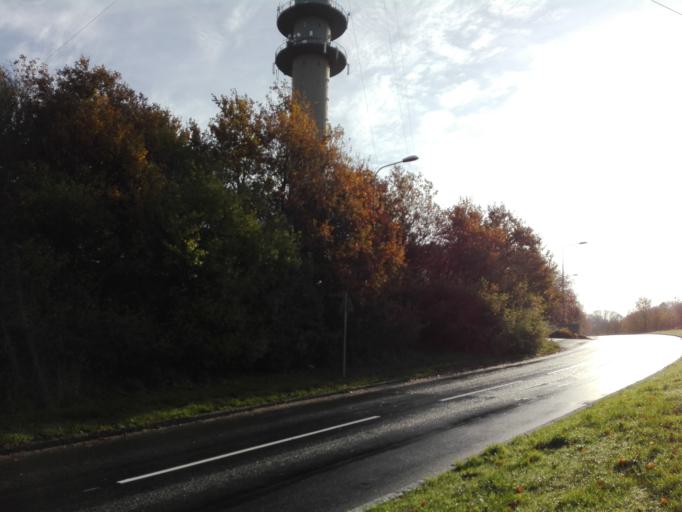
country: DK
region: Central Jutland
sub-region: Arhus Kommune
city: Beder
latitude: 56.0994
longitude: 10.2154
